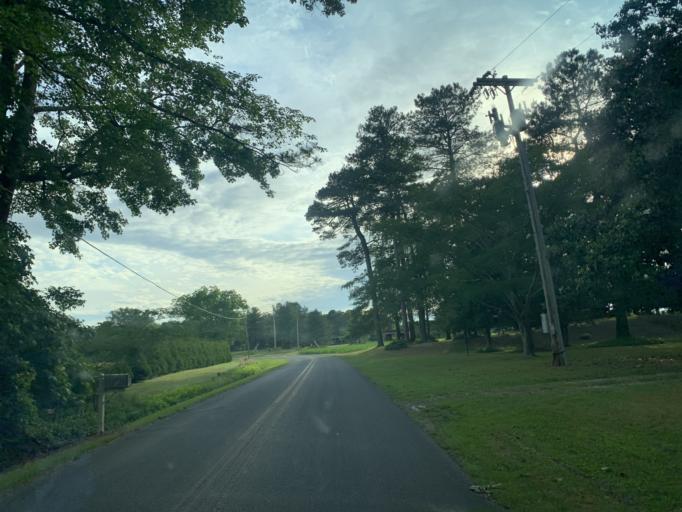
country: US
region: Maryland
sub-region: Worcester County
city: Pocomoke City
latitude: 38.0811
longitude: -75.4746
